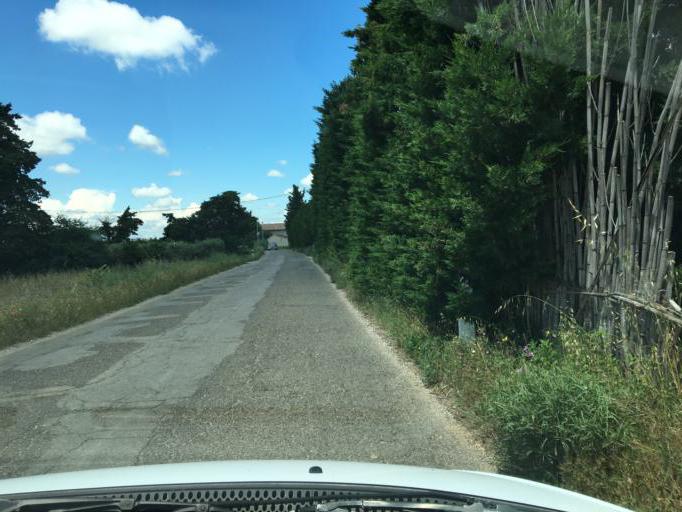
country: FR
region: Provence-Alpes-Cote d'Azur
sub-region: Departement du Vaucluse
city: Carpentras
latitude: 44.0366
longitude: 5.0569
